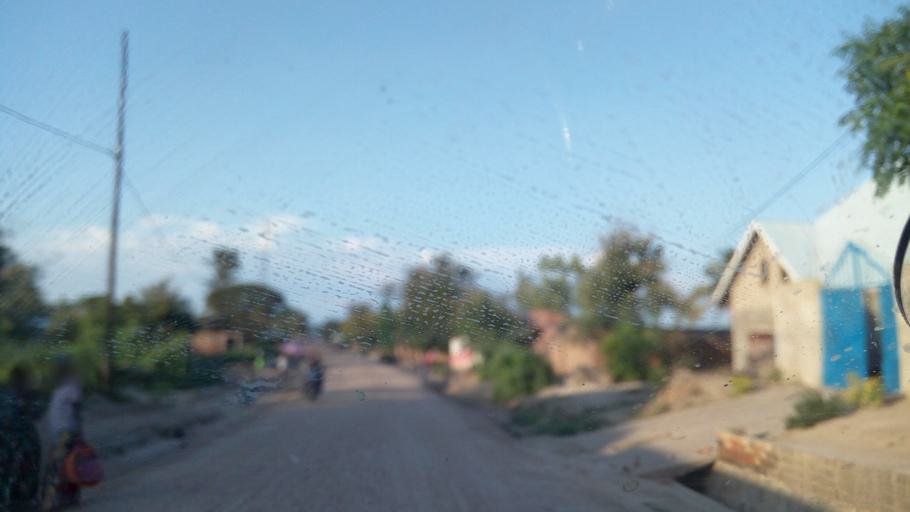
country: BI
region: Bururi
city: Rumonge
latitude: -4.1123
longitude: 29.0886
